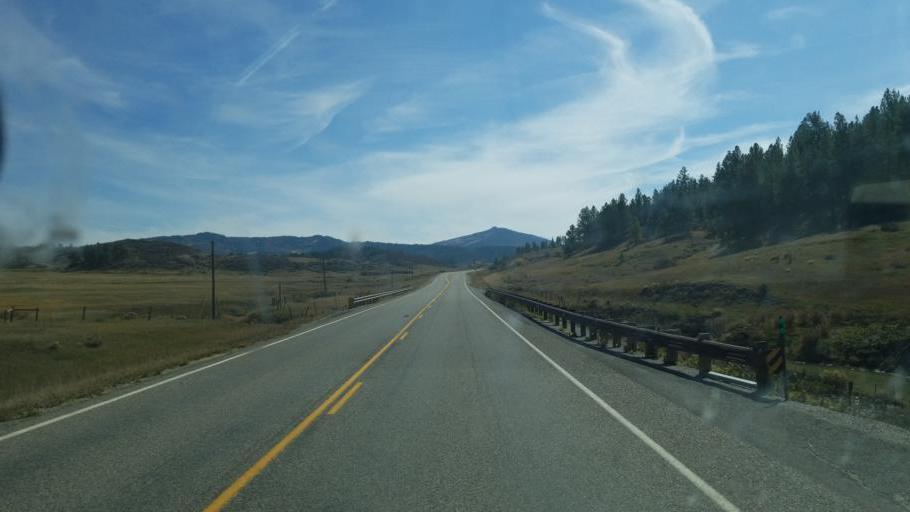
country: US
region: New Mexico
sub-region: Rio Arriba County
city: Dulce
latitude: 37.0173
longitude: -106.8107
